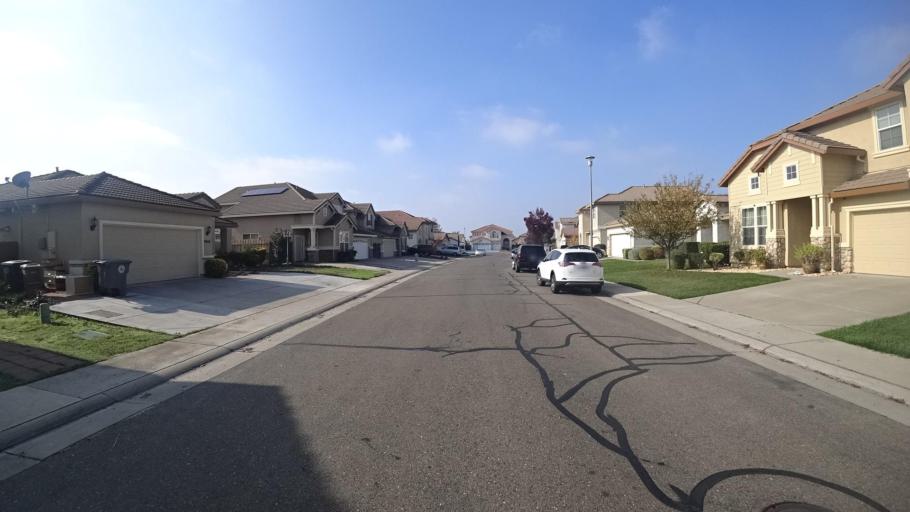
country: US
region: California
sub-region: Sacramento County
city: Vineyard
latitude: 38.4439
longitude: -121.3665
